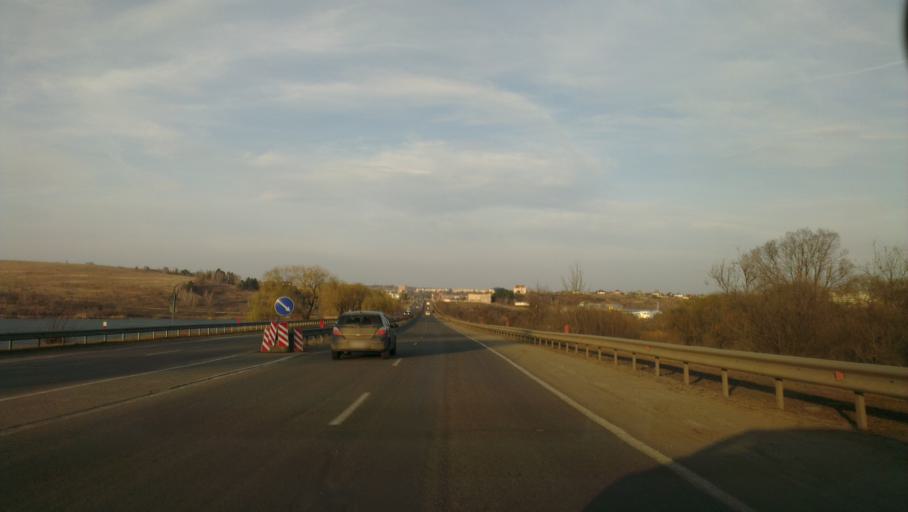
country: MD
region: Laloveni
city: Ialoveni
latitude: 46.9531
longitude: 28.7401
